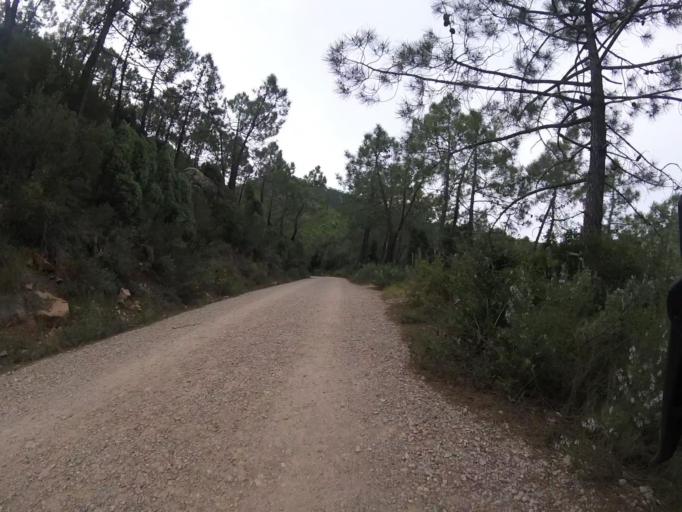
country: ES
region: Valencia
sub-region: Provincia de Castello
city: Cabanes
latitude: 40.0996
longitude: 0.0340
